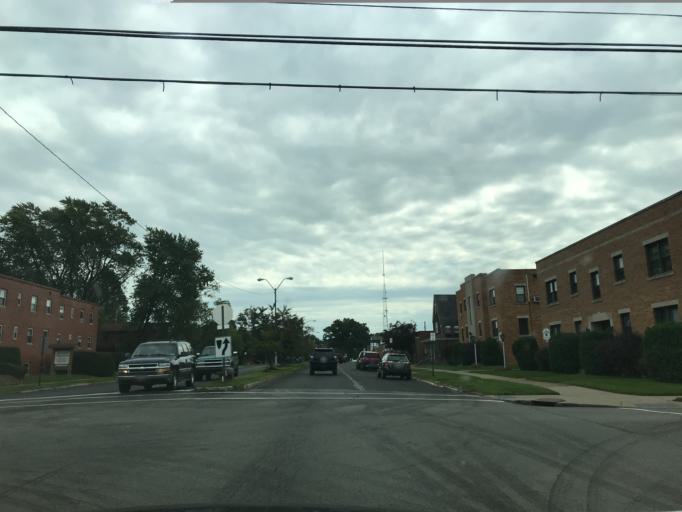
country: US
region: Pennsylvania
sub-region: Erie County
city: Erie
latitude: 42.1087
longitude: -80.0715
